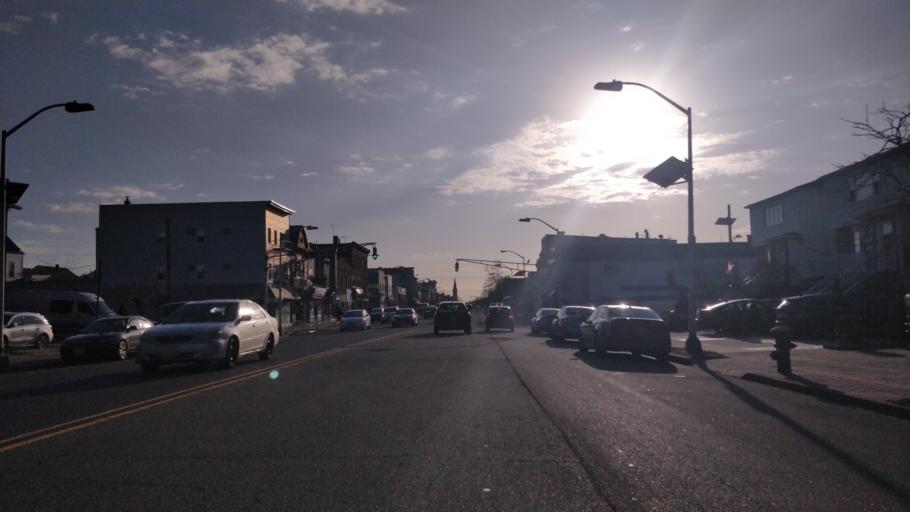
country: US
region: New Jersey
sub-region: Hudson County
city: Bayonne
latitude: 40.6648
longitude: -74.1209
